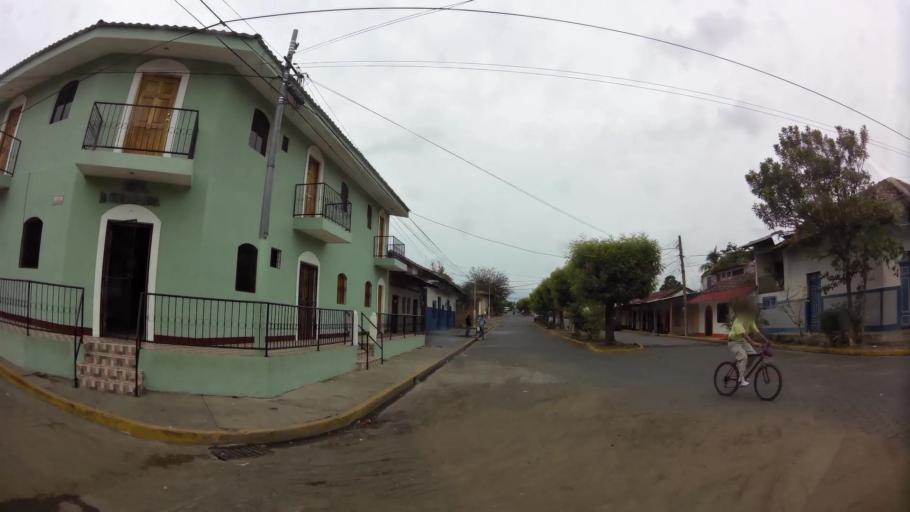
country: NI
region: Granada
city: Granada
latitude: 11.9319
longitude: -85.9601
